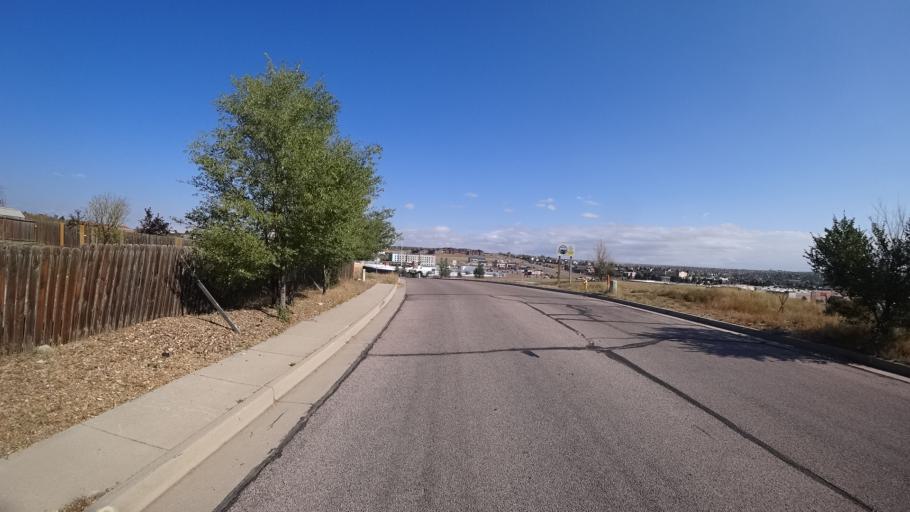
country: US
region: Colorado
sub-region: El Paso County
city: Cimarron Hills
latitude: 38.8904
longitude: -104.7227
